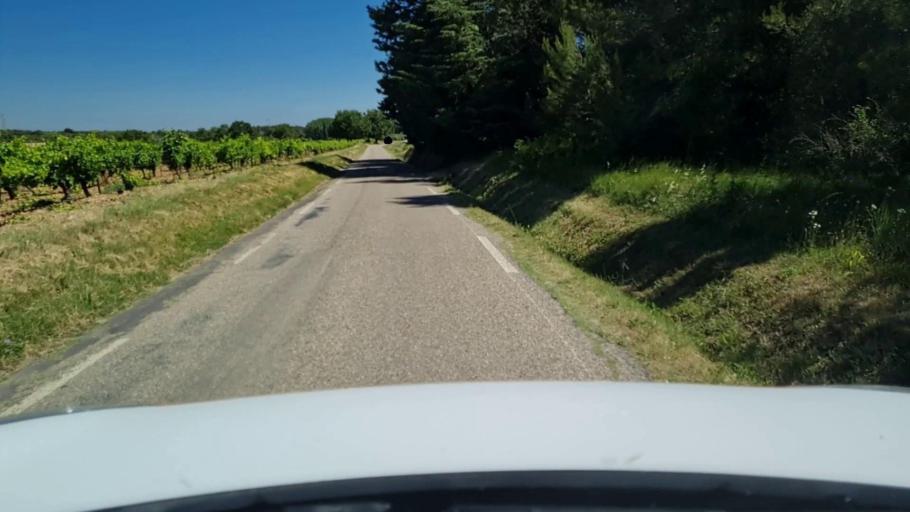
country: FR
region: Languedoc-Roussillon
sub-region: Departement du Gard
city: Saint-Mamert-du-Gard
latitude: 43.8568
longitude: 4.1620
